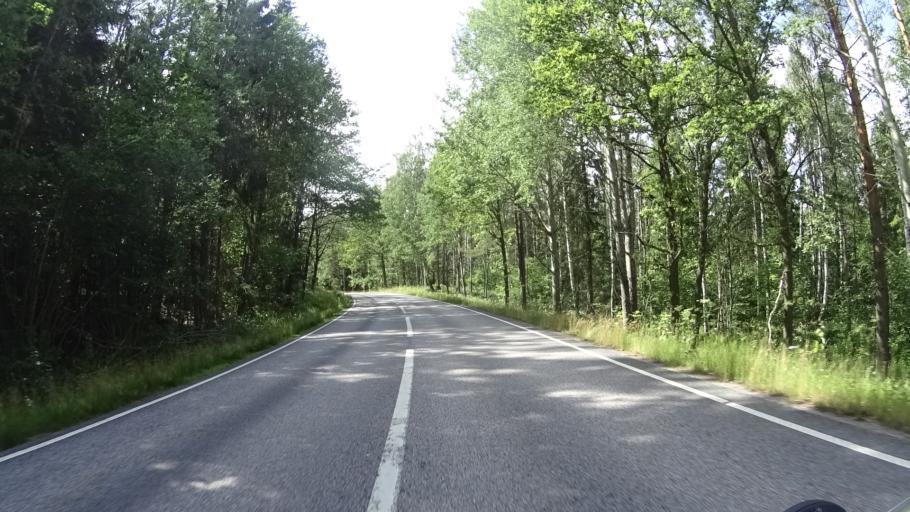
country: SE
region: Kalmar
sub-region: Vasterviks Kommun
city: Overum
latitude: 58.0796
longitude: 16.1808
